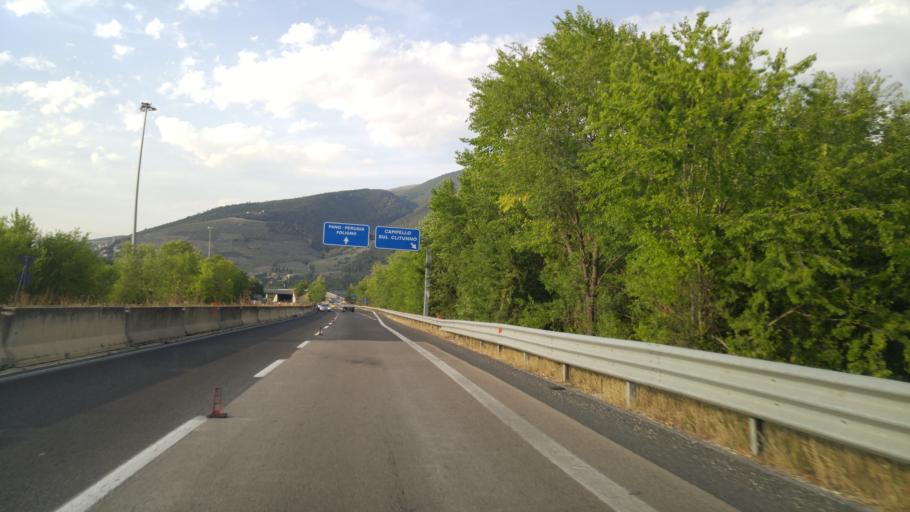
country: IT
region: Umbria
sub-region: Provincia di Perugia
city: Campello sul Clitunno
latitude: 42.8228
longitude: 12.7593
